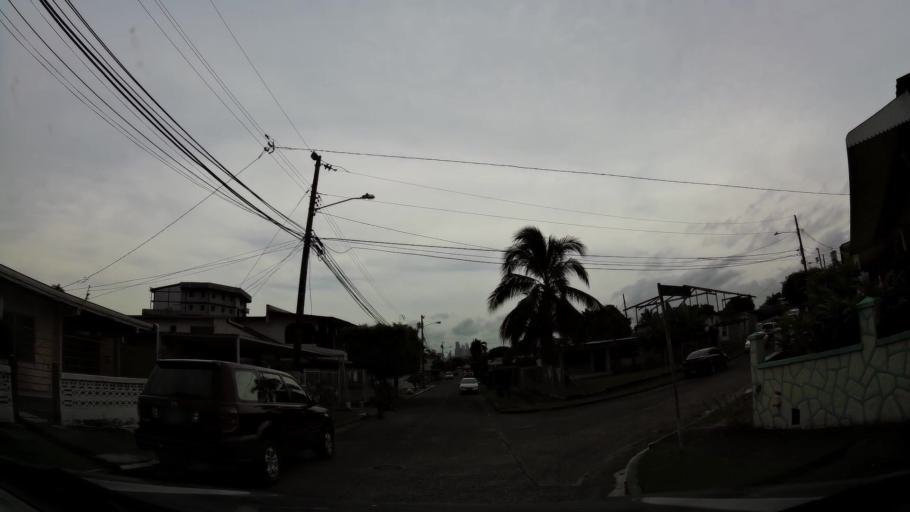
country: PA
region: Panama
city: Panama
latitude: 9.0148
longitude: -79.5231
